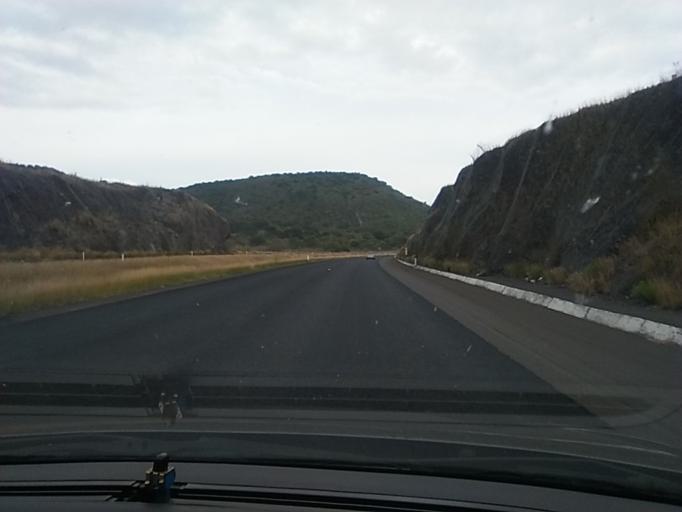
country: MX
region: Mexico
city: Huaniqueo de Morales
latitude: 19.8870
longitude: -101.4613
